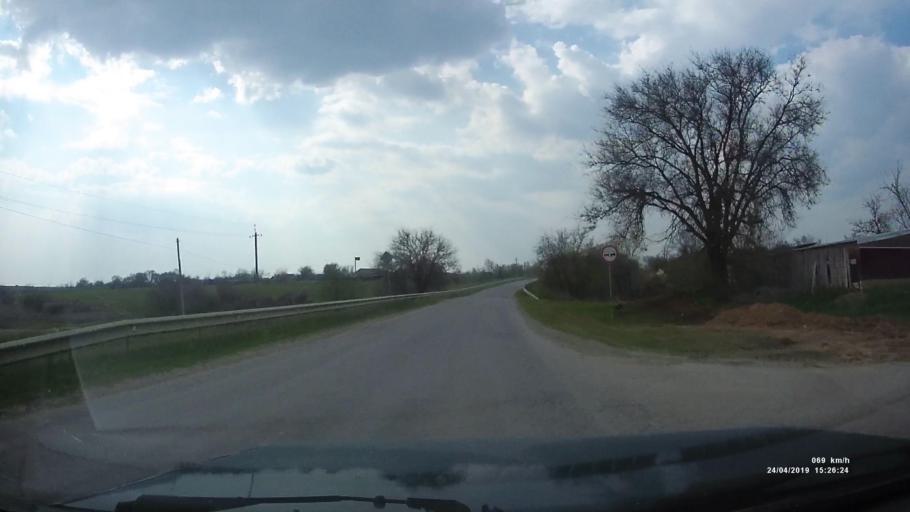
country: RU
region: Rostov
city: Remontnoye
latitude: 46.5581
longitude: 43.0329
